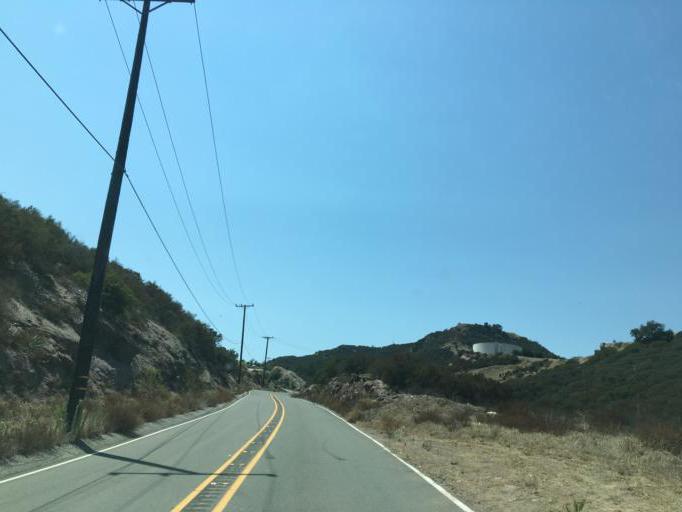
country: US
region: California
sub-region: Los Angeles County
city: Las Flores
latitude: 34.0792
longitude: -118.6467
